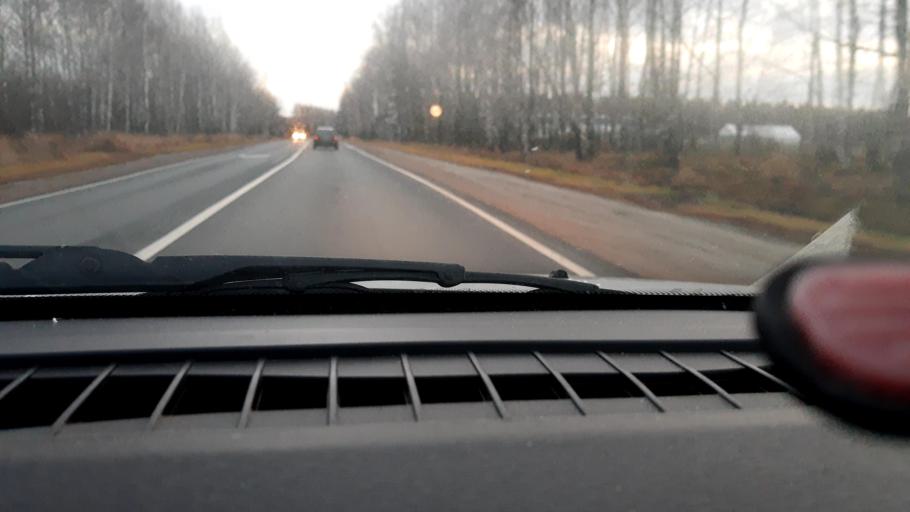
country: RU
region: Nizjnij Novgorod
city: Krasnyye Baki
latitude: 57.0575
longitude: 45.1364
